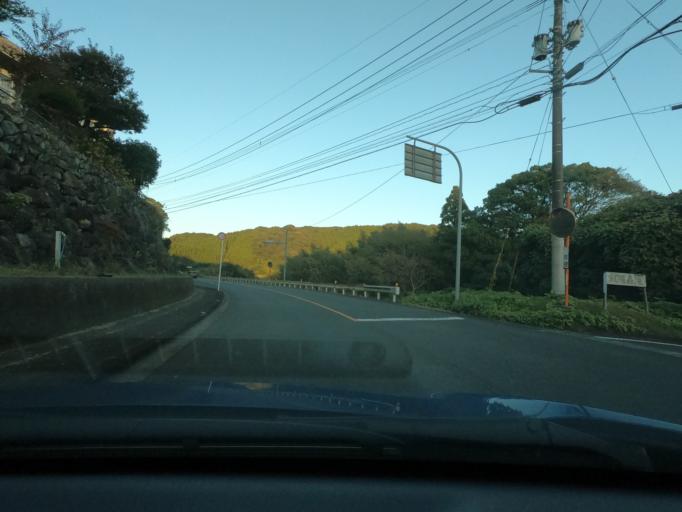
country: JP
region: Kagoshima
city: Satsumasendai
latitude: 31.7909
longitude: 130.4706
